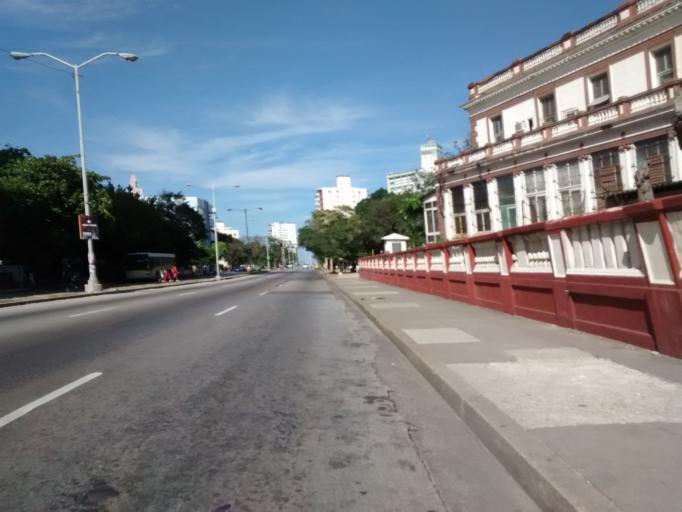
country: CU
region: La Habana
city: Havana
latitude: 23.1419
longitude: -82.3906
